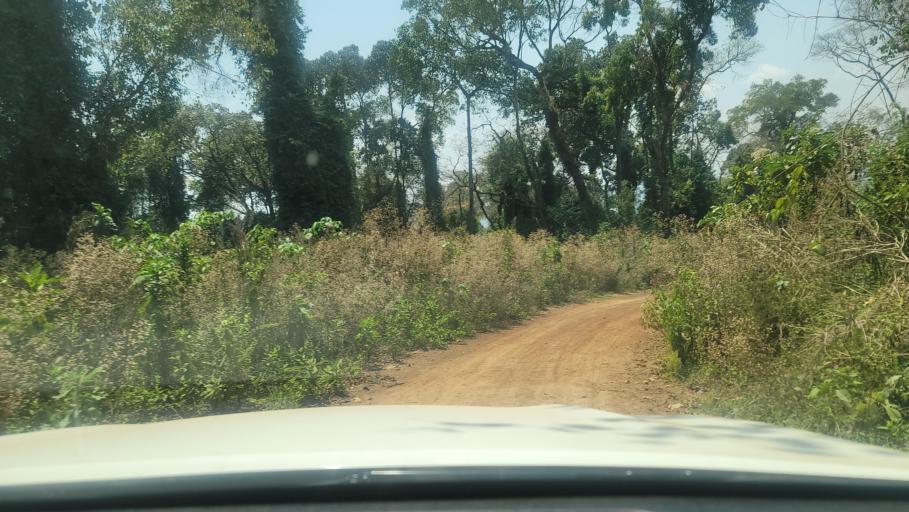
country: ET
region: Southern Nations, Nationalities, and People's Region
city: Bonga
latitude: 7.5484
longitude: 36.1754
